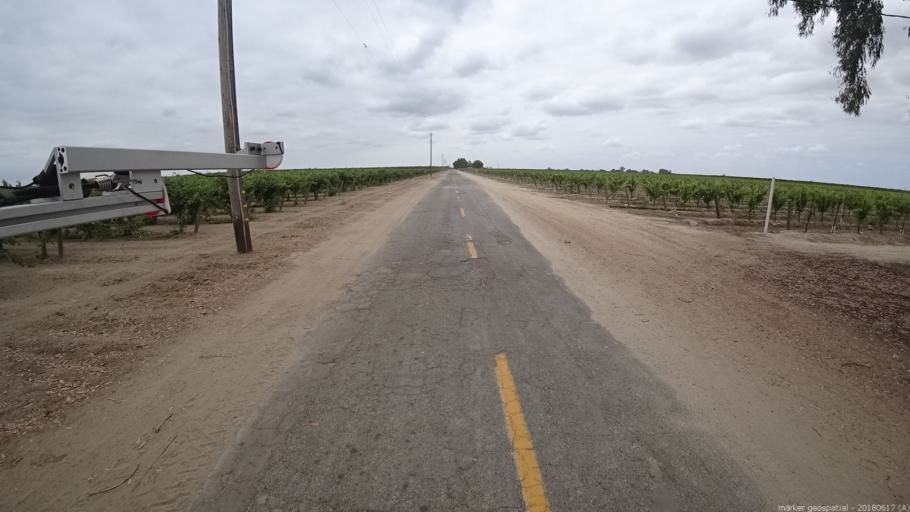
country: US
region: California
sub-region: Madera County
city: Madera
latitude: 36.9193
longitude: -120.1559
